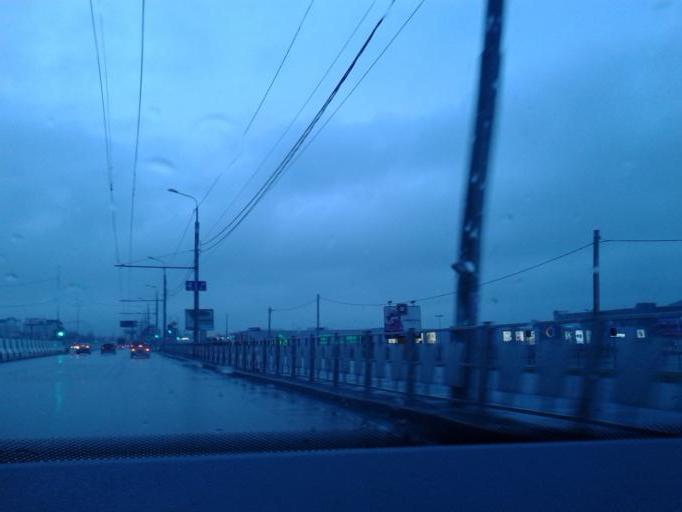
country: RU
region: Volgograd
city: Volgograd
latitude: 48.6351
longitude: 44.4300
